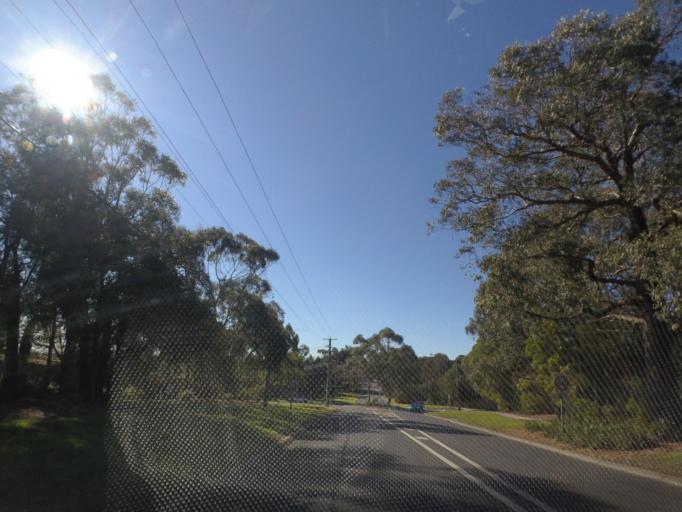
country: AU
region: Victoria
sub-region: Maroondah
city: Croydon Hills
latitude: -37.7752
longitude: 145.2754
